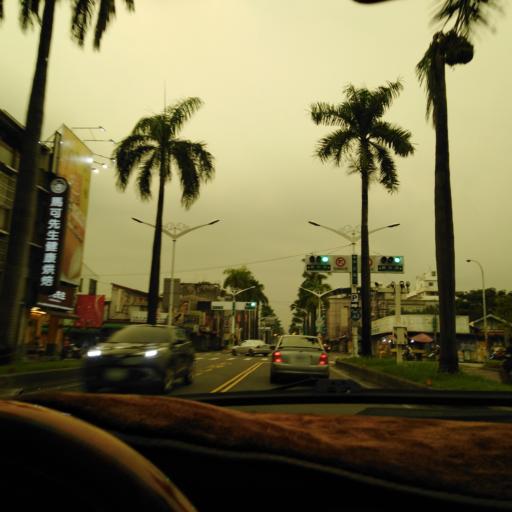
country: TW
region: Taiwan
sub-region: Pingtung
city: Pingtung
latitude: 22.6783
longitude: 120.4909
